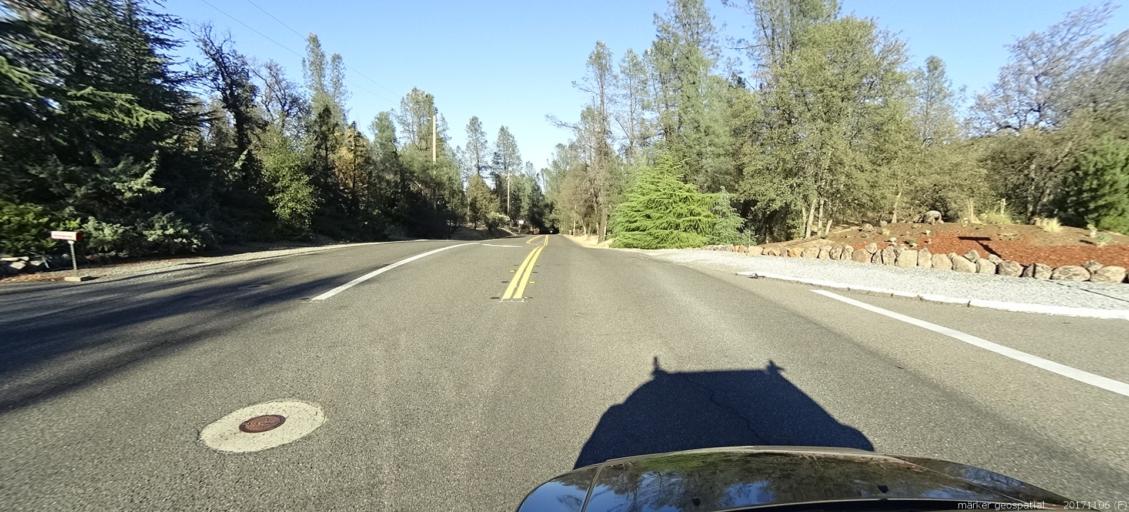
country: US
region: California
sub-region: Shasta County
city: Shasta
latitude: 40.5766
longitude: -122.4560
